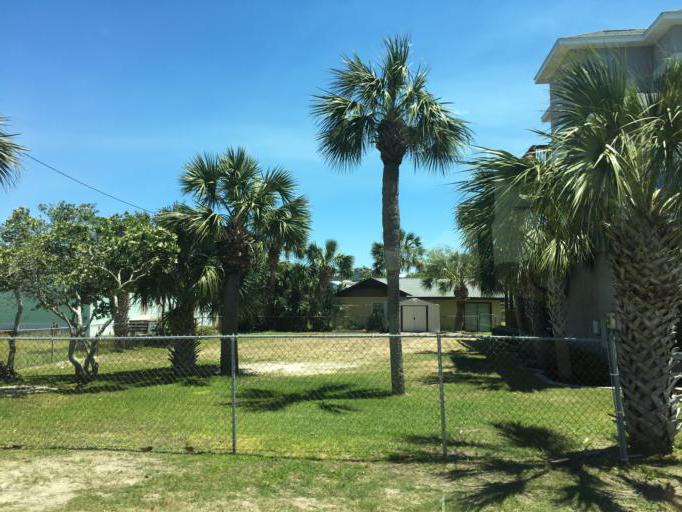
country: US
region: Florida
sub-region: Bay County
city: Laguna Beach
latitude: 30.2408
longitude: -85.9239
